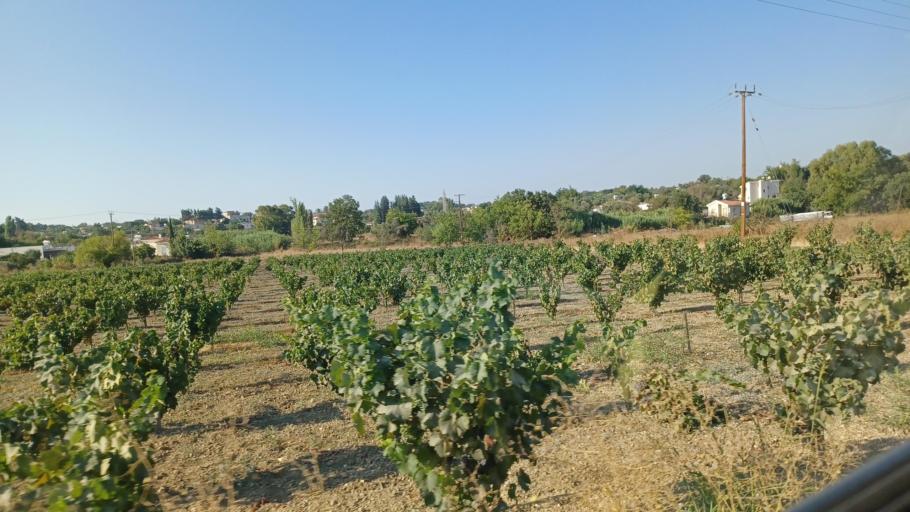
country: CY
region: Pafos
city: Mesogi
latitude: 34.8916
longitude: 32.5070
